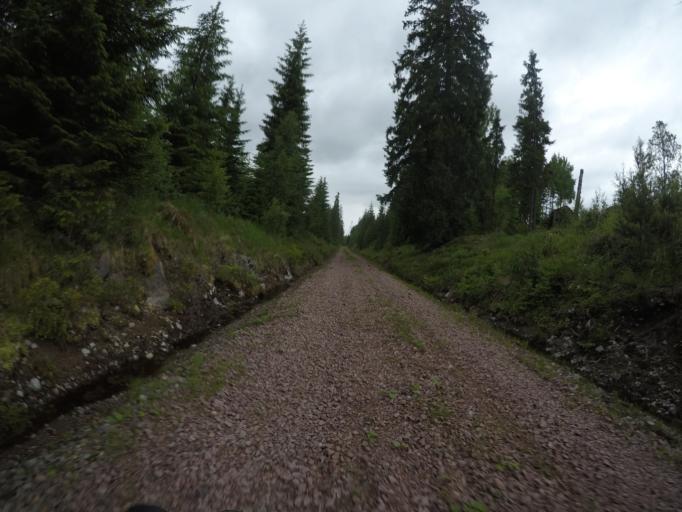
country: SE
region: OErebro
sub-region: Hallefors Kommun
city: Haellefors
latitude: 60.0222
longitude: 14.5779
